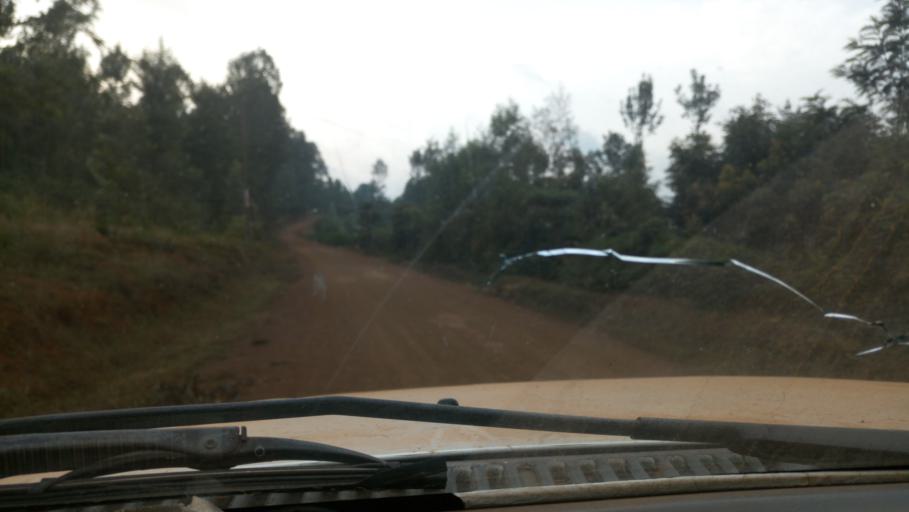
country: KE
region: Murang'a District
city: Kangema
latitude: -0.7204
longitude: 37.0089
